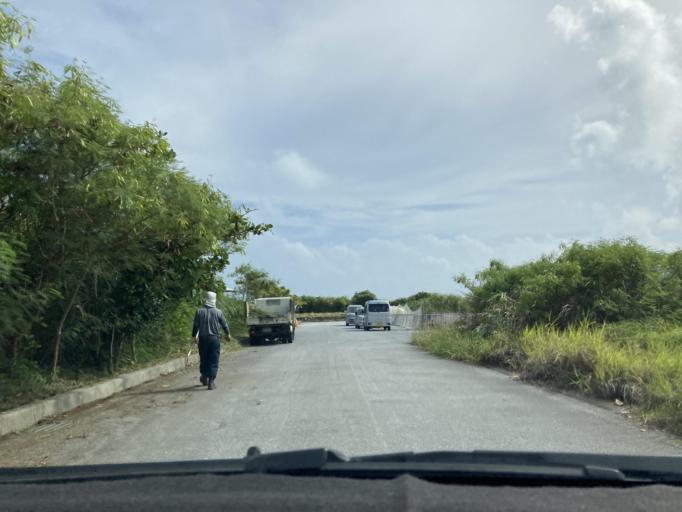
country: JP
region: Okinawa
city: Ginowan
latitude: 26.1494
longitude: 127.8096
